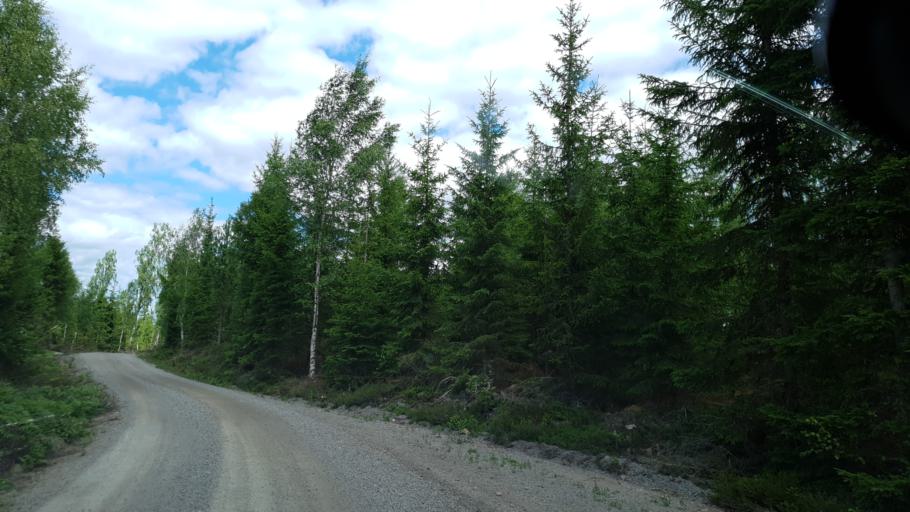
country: SE
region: Kalmar
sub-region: Hultsfreds Kommun
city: Virserum
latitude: 57.0872
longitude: 15.6206
